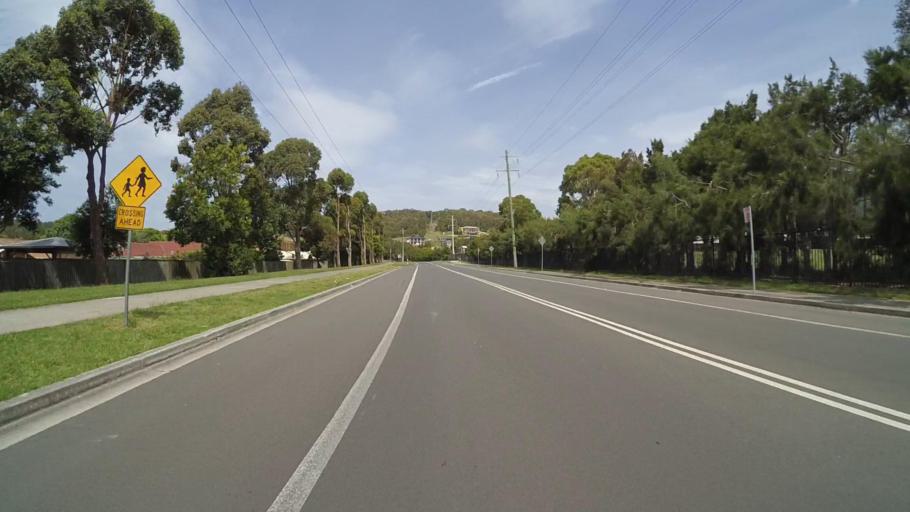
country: AU
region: New South Wales
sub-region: Shellharbour
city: Albion Park Rail
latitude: -34.5913
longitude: 150.7812
